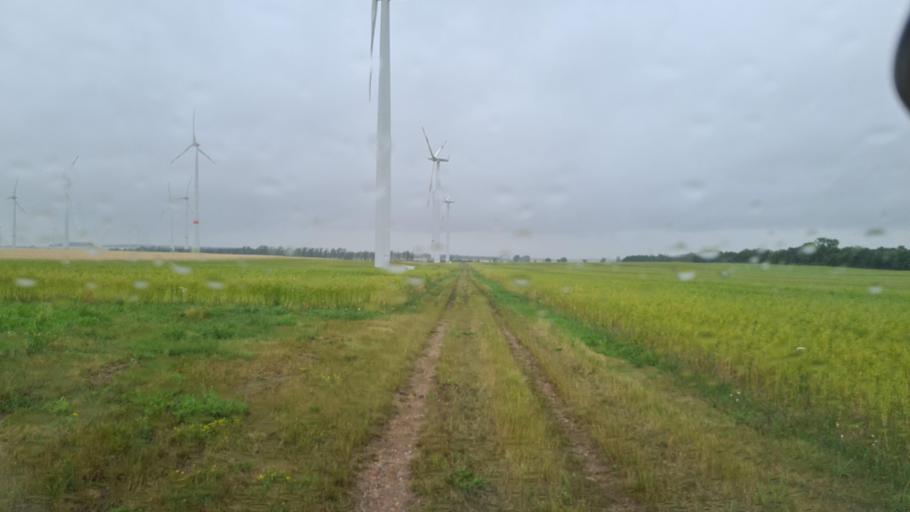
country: DE
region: Brandenburg
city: Juterbog
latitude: 51.9475
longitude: 13.1830
